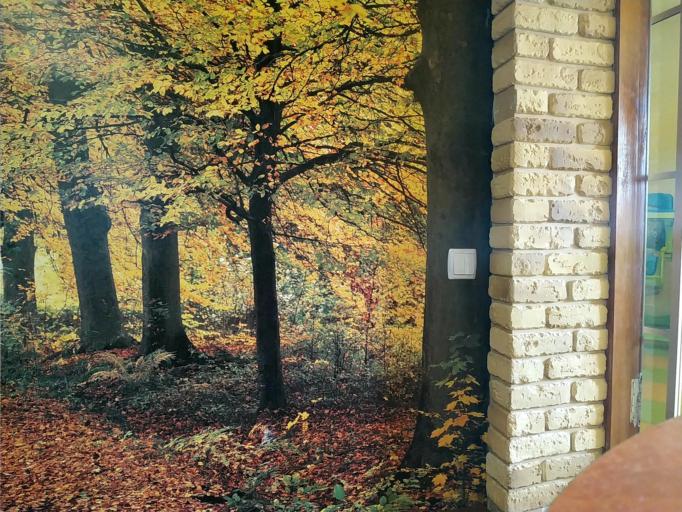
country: RU
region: Smolensk
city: Katyn'
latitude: 54.8822
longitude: 31.8046
